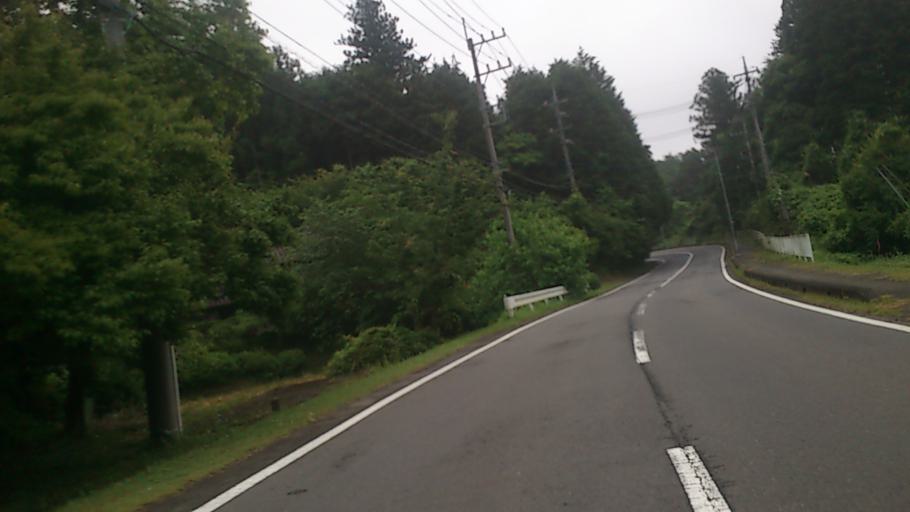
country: JP
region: Ibaraki
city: Omiya
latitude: 36.6301
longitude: 140.3791
